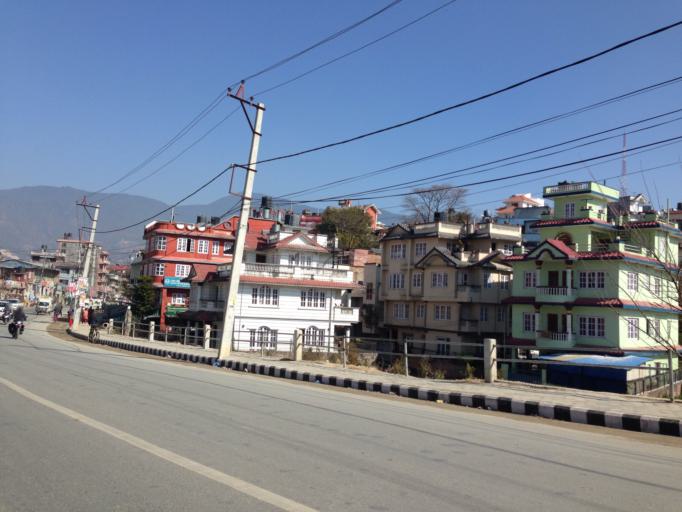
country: NP
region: Central Region
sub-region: Bagmati Zone
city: Kathmandu
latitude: 27.7499
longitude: 85.3455
